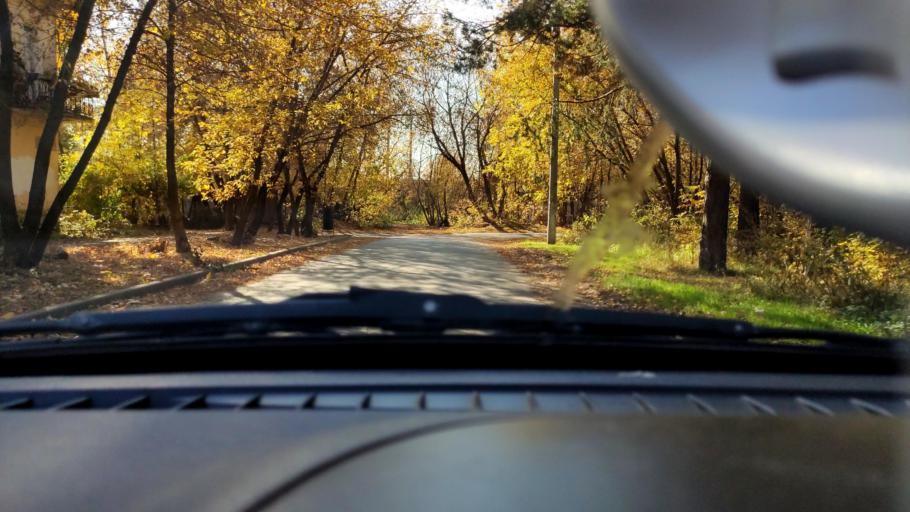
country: RU
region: Perm
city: Kondratovo
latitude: 58.0412
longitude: 56.0983
